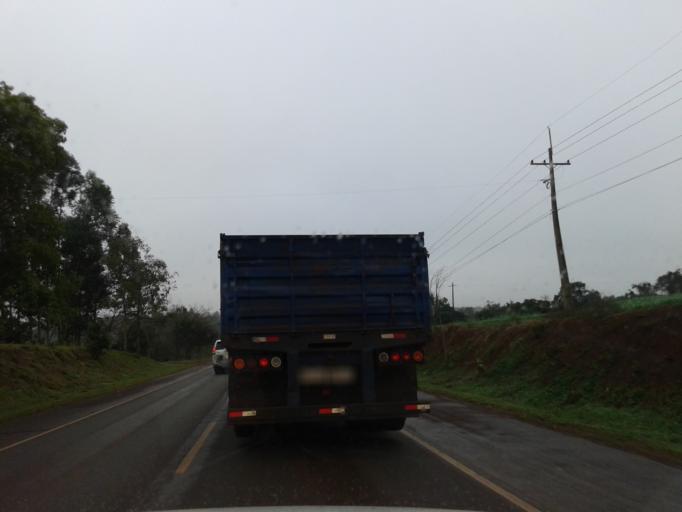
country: PY
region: Alto Parana
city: Naranjal
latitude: -25.9563
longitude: -55.1217
